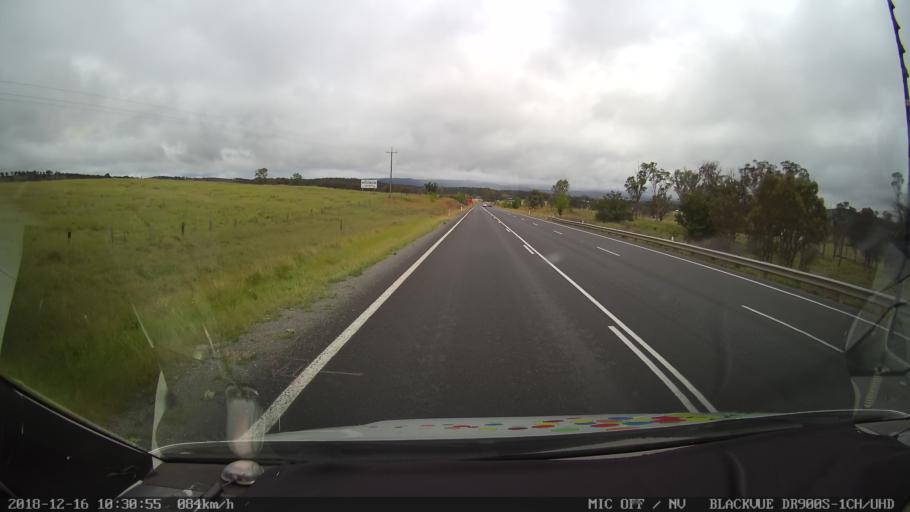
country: AU
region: New South Wales
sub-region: Tenterfield Municipality
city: Carrolls Creek
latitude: -29.0868
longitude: 152.0037
